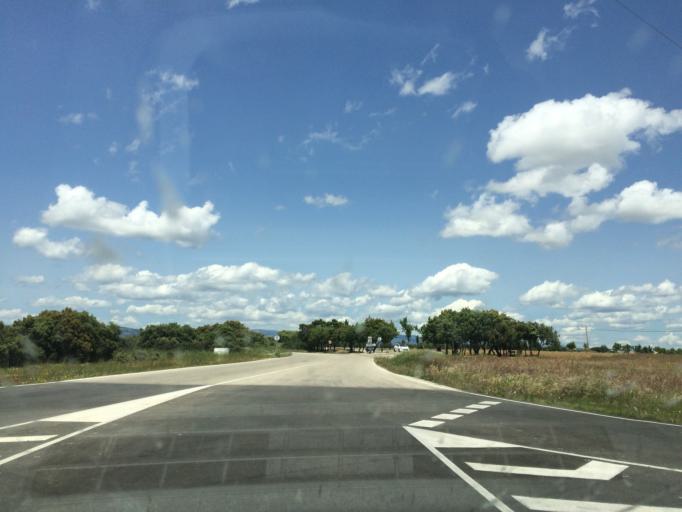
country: ES
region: Madrid
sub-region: Provincia de Madrid
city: Valdepielagos
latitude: 40.7539
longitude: -3.4119
